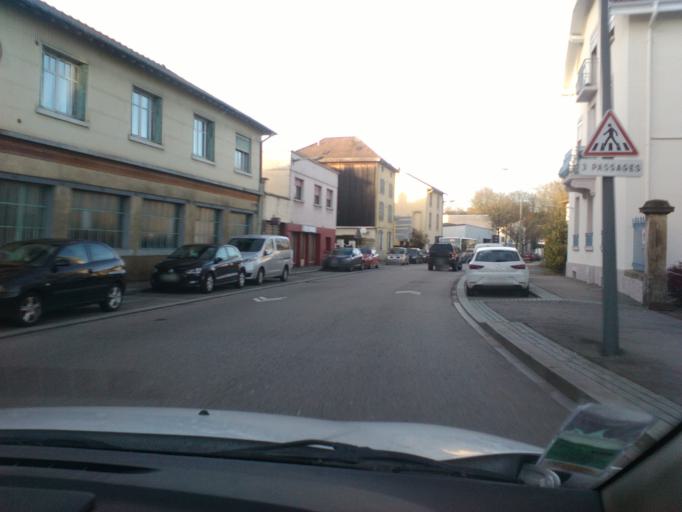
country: FR
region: Lorraine
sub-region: Departement des Vosges
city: Epinal
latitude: 48.1844
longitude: 6.4413
